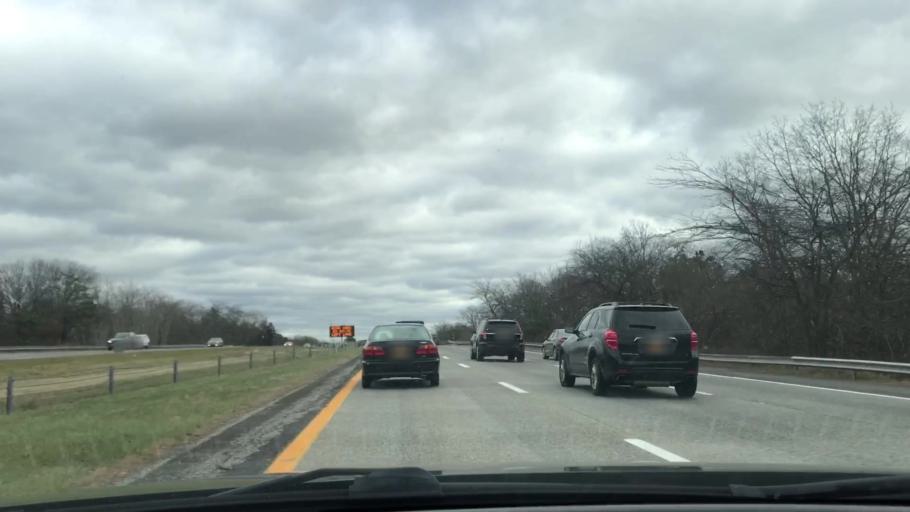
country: US
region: New York
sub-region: Suffolk County
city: Shirley
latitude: 40.8508
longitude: -72.8635
